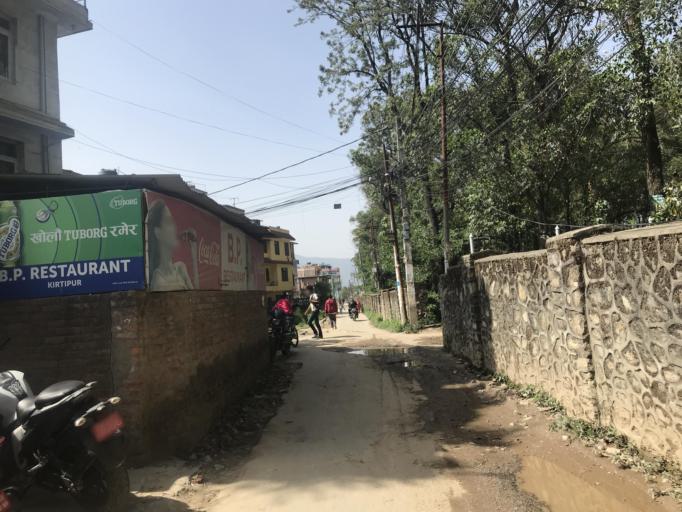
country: NP
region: Central Region
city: Kirtipur
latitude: 27.6809
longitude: 85.2816
